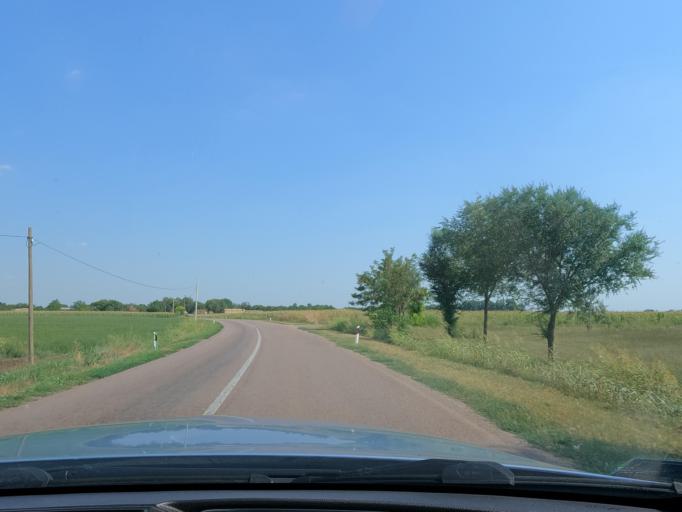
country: RS
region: Autonomna Pokrajina Vojvodina
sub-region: Severnobacki Okrug
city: Mali Igos
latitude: 45.7653
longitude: 19.7420
